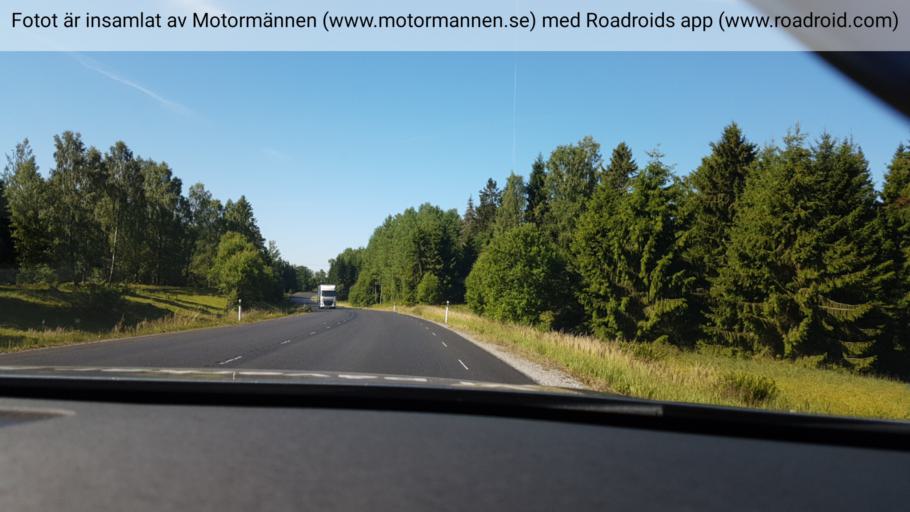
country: SE
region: Vaestra Goetaland
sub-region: Ulricehamns Kommun
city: Ulricehamn
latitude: 57.9433
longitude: 13.5122
